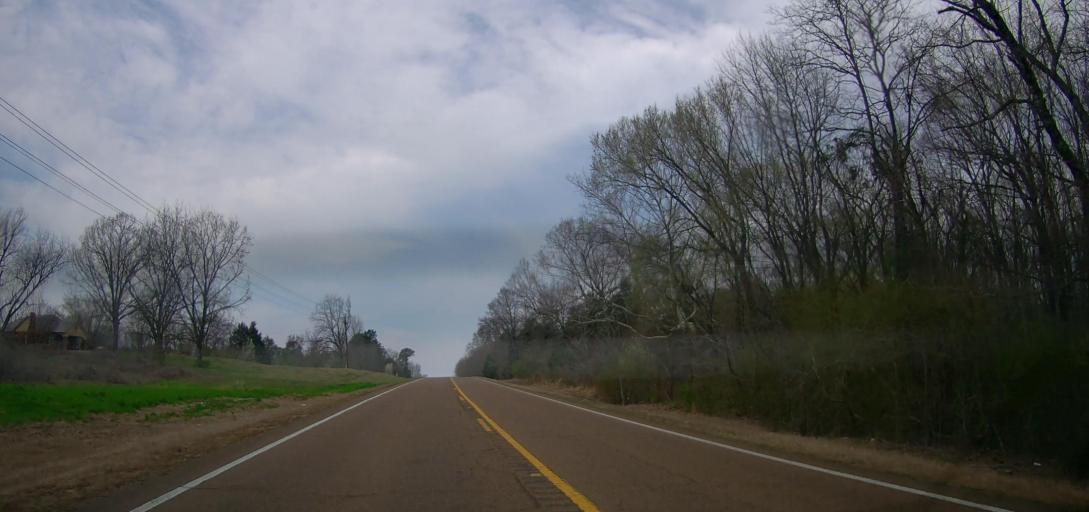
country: US
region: Mississippi
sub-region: Marshall County
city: Byhalia
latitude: 34.8493
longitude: -89.6289
